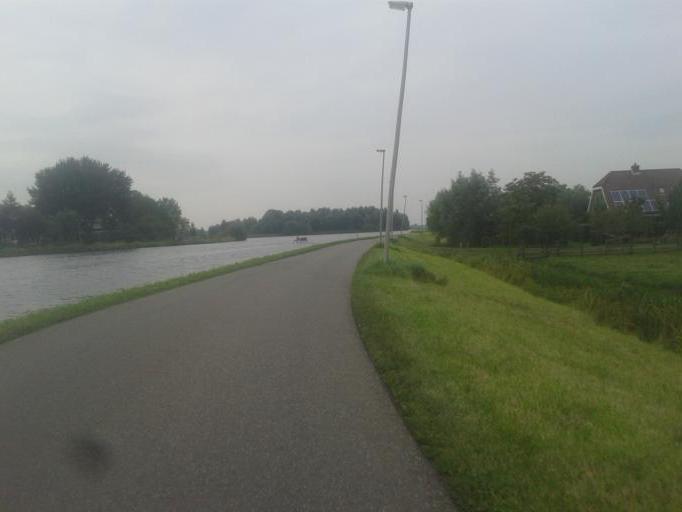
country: NL
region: South Holland
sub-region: Gemeente Leiderdorp
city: Leiderdorp
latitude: 52.1792
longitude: 4.5182
